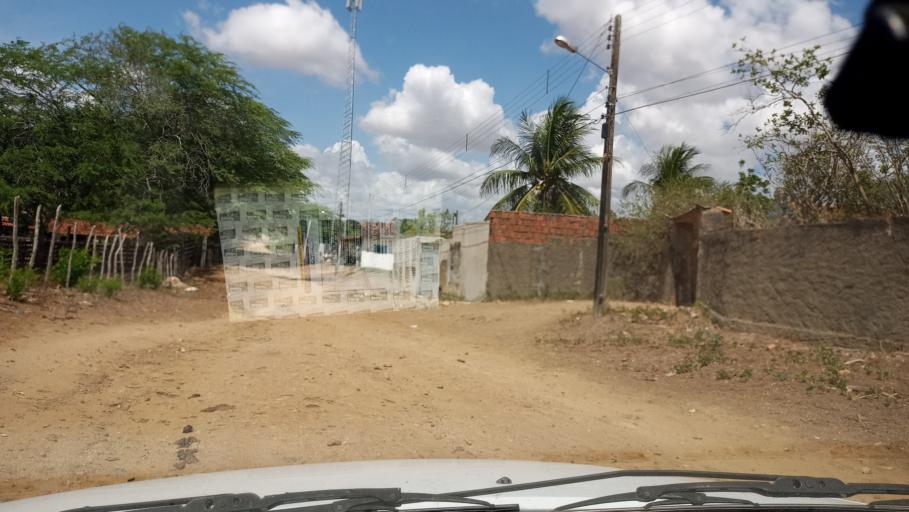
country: BR
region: Rio Grande do Norte
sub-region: Santo Antonio
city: Santo Antonio
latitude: -6.3483
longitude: -35.3715
